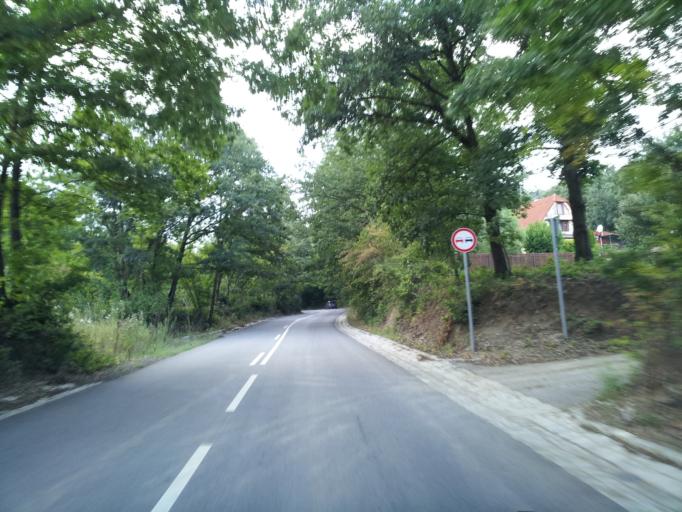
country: HU
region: Pest
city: Kismaros
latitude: 47.8317
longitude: 18.9668
